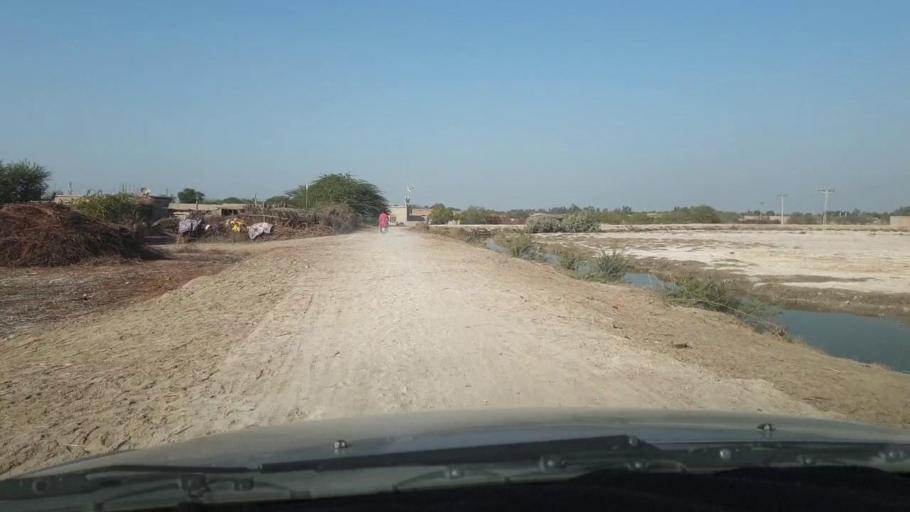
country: PK
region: Sindh
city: Mirpur Mathelo
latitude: 27.9739
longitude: 69.5603
